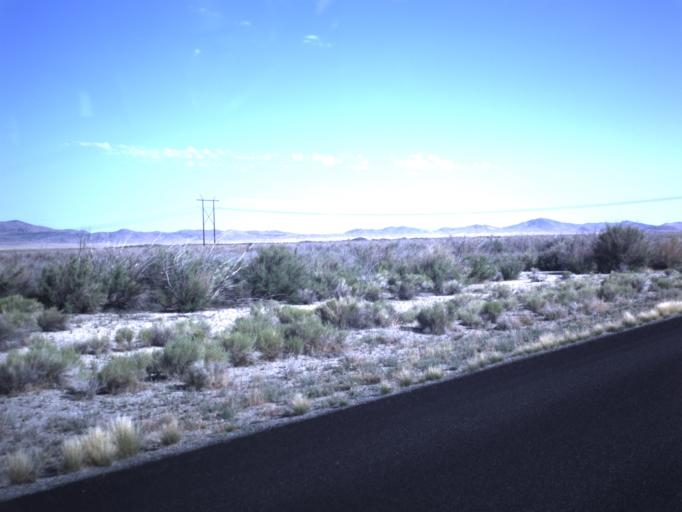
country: US
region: Utah
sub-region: Beaver County
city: Milford
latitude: 38.5689
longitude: -112.9902
